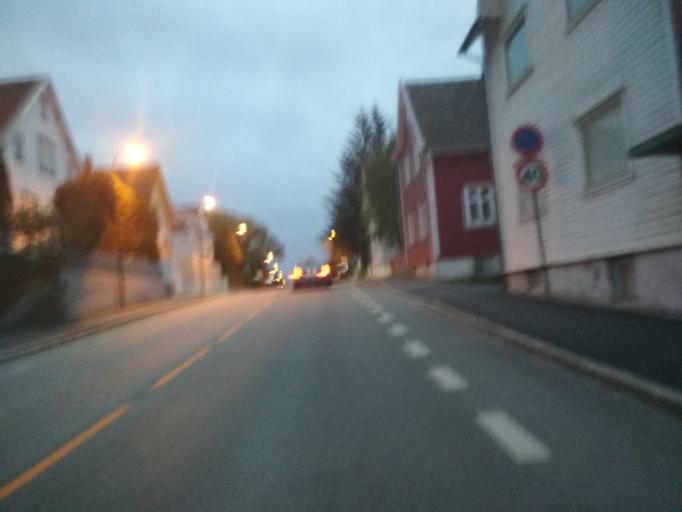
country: NO
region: Rogaland
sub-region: Stavanger
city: Stavanger
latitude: 58.9775
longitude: 5.7163
